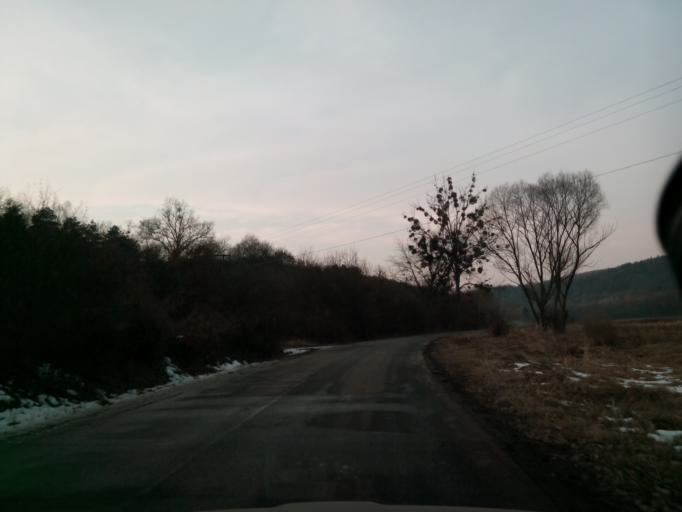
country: HU
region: Borsod-Abauj-Zemplen
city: Gonc
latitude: 48.4965
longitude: 21.3421
